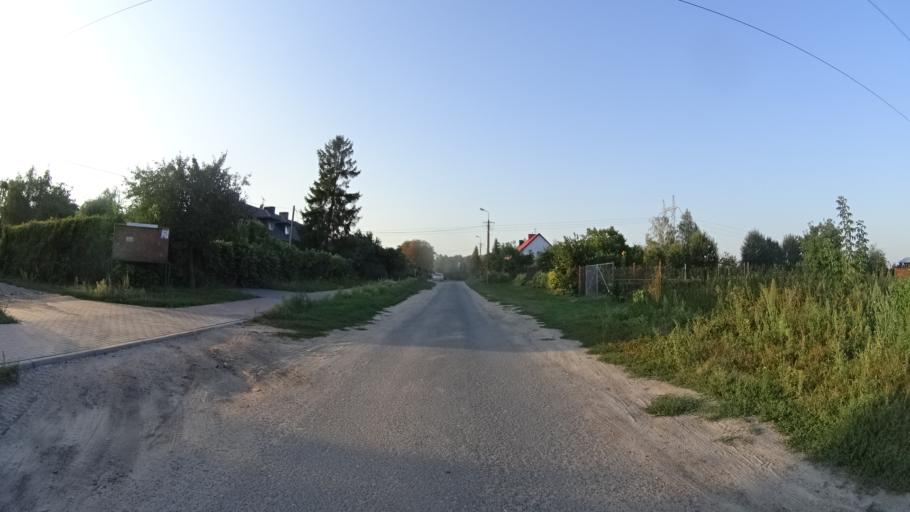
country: PL
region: Masovian Voivodeship
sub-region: Powiat warszawski zachodni
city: Ozarow Mazowiecki
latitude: 52.2372
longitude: 20.7812
